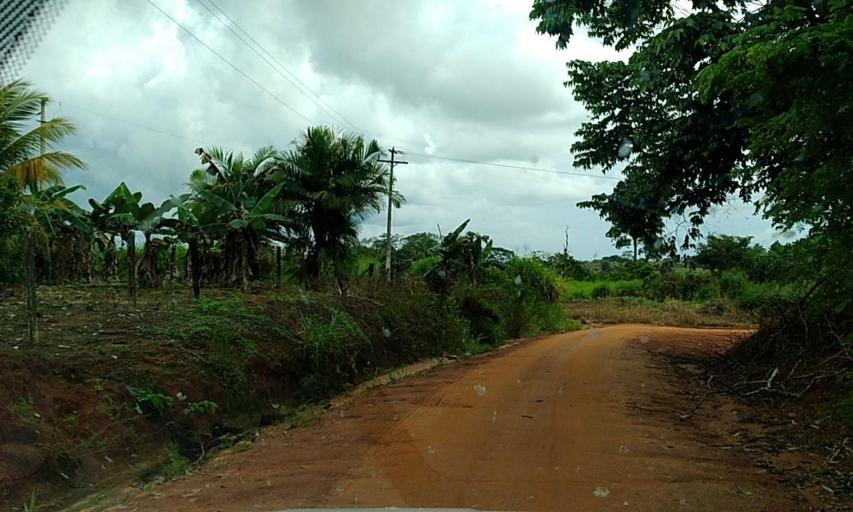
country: BR
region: Para
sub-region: Altamira
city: Altamira
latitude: -3.3037
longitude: -52.6870
